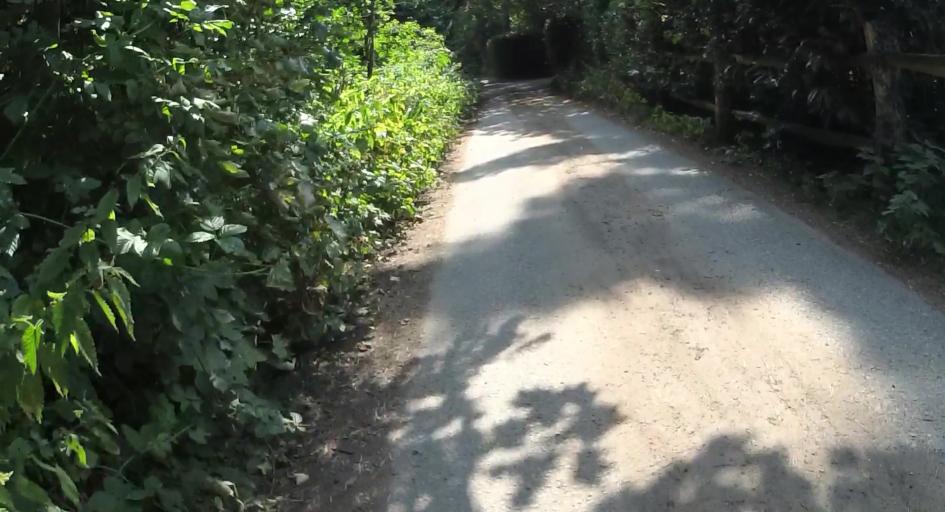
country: GB
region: England
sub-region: Surrey
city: Farnham
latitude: 51.1940
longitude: -0.7836
